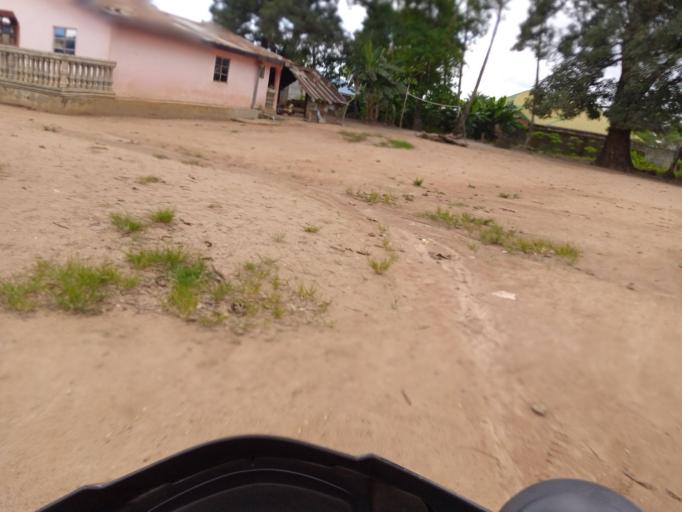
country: SL
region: Northern Province
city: Masoyila
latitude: 8.5762
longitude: -13.1625
